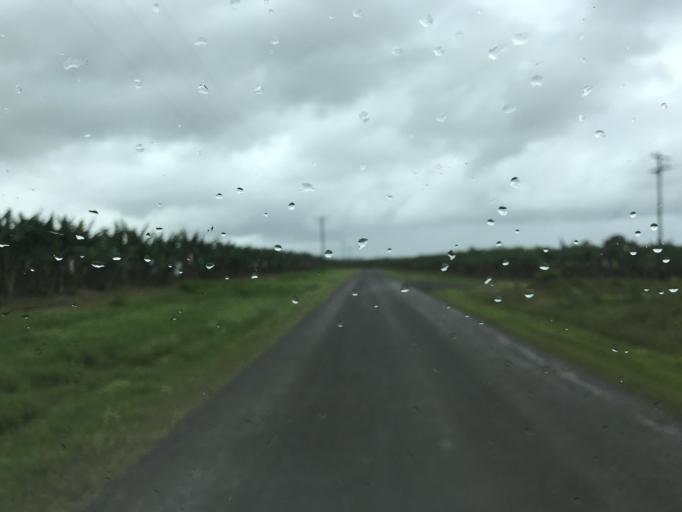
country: AU
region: Queensland
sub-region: Cassowary Coast
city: Innisfail
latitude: -17.5074
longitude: 145.9794
